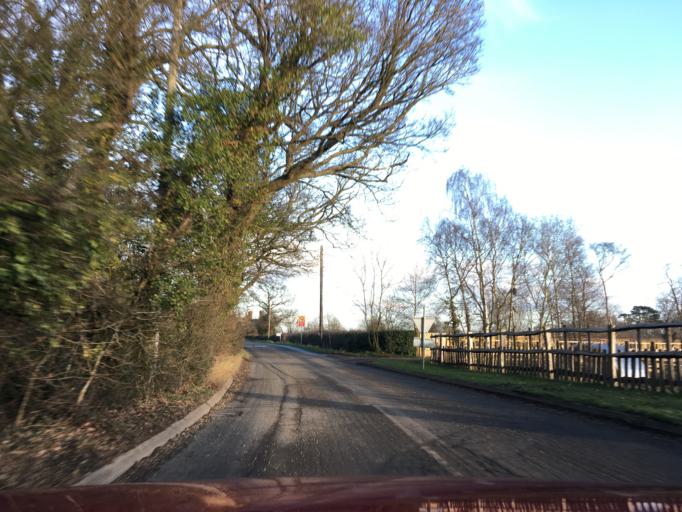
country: GB
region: England
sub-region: Warwickshire
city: Stratford-upon-Avon
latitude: 52.2289
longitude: -1.6954
